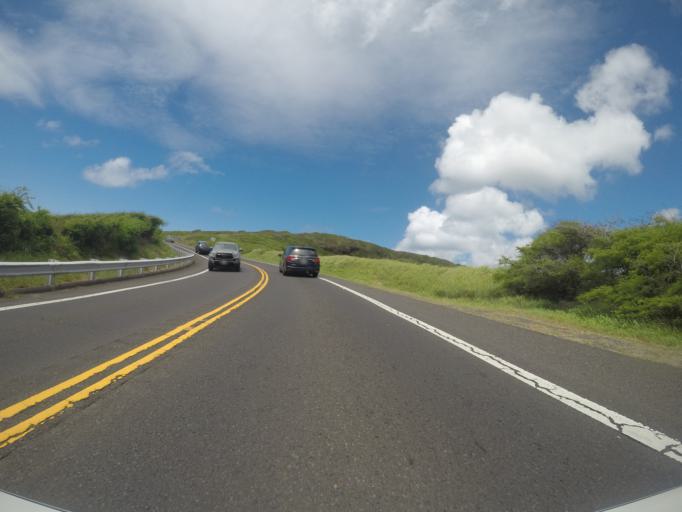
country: US
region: Hawaii
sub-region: Honolulu County
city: Waimanalo Beach
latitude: 21.2765
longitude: -157.6876
